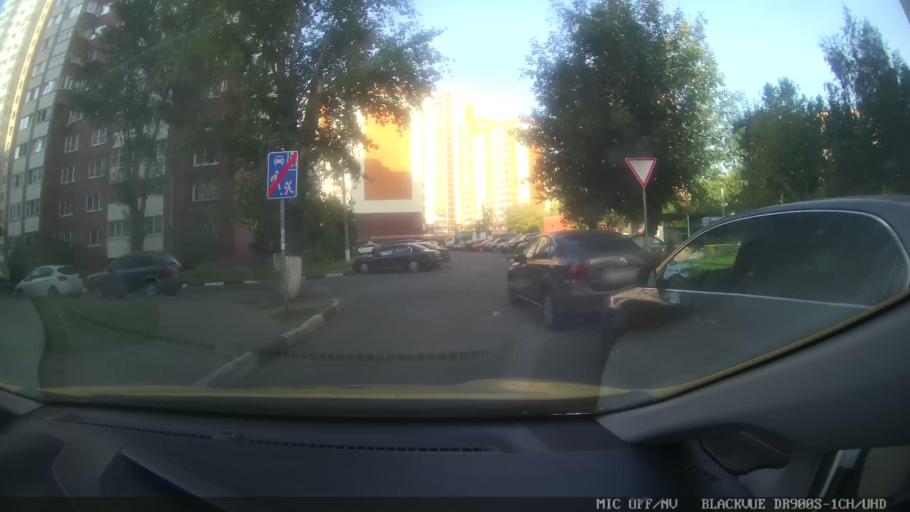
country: RU
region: Moskovskaya
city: Reutov
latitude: 55.7498
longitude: 37.8744
